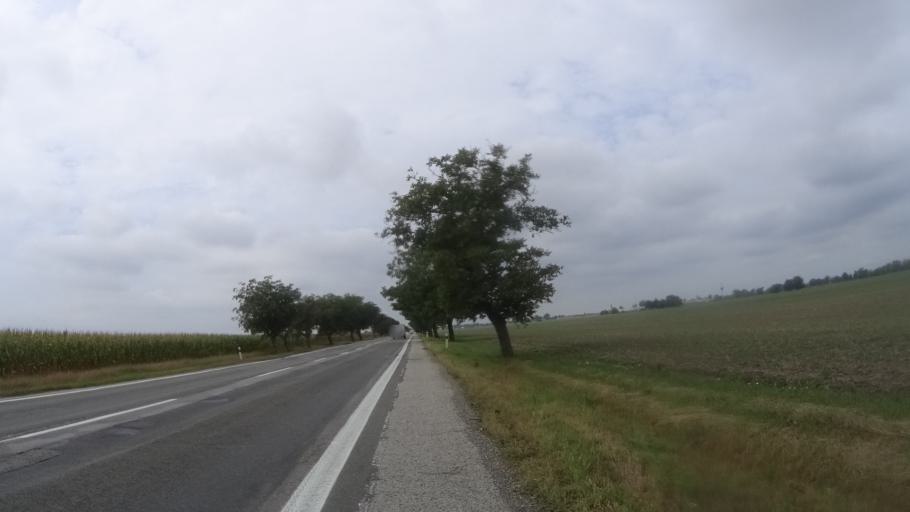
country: HU
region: Komarom-Esztergom
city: Acs
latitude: 47.7666
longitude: 18.0100
